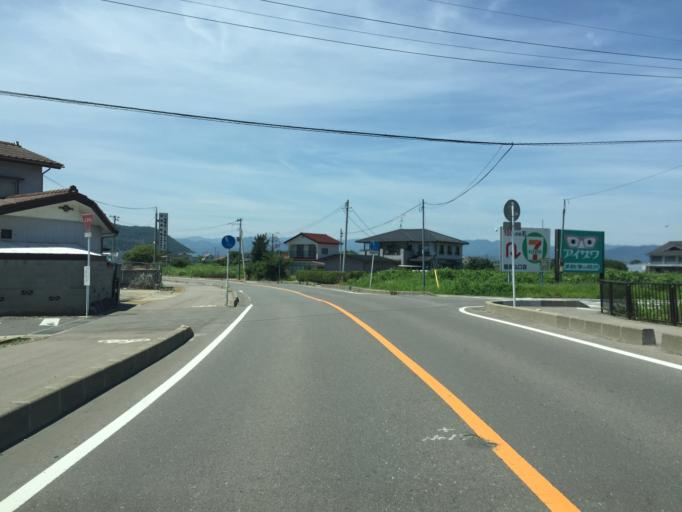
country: JP
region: Fukushima
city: Fukushima-shi
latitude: 37.7718
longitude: 140.5084
